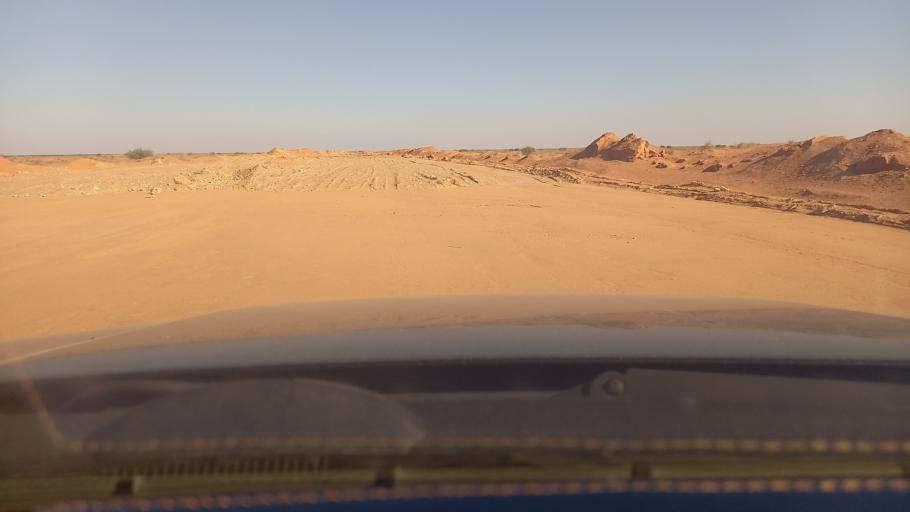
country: TN
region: Madanin
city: Medenine
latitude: 33.1606
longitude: 10.5185
